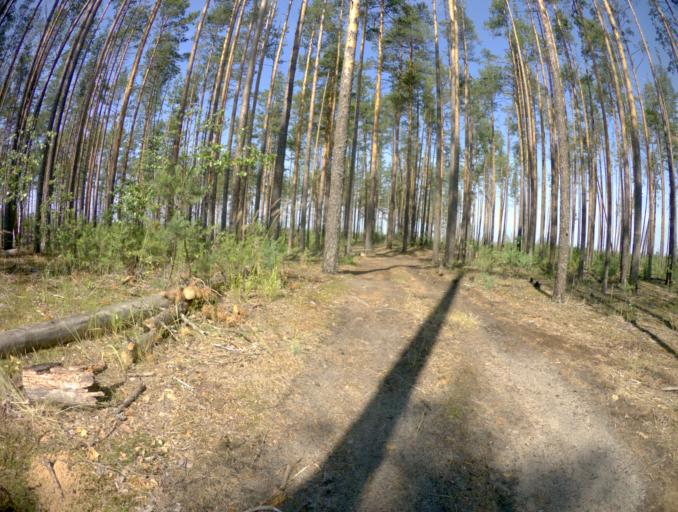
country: RU
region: Ivanovo
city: Talitsy
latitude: 56.4124
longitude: 42.2735
